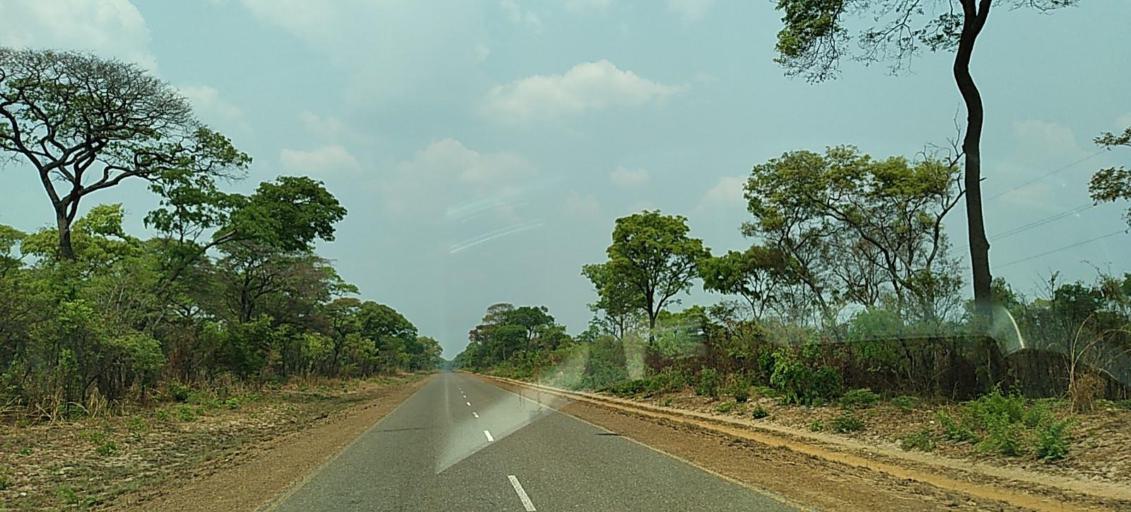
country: ZM
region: North-Western
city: Zambezi
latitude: -13.5568
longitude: 23.1915
